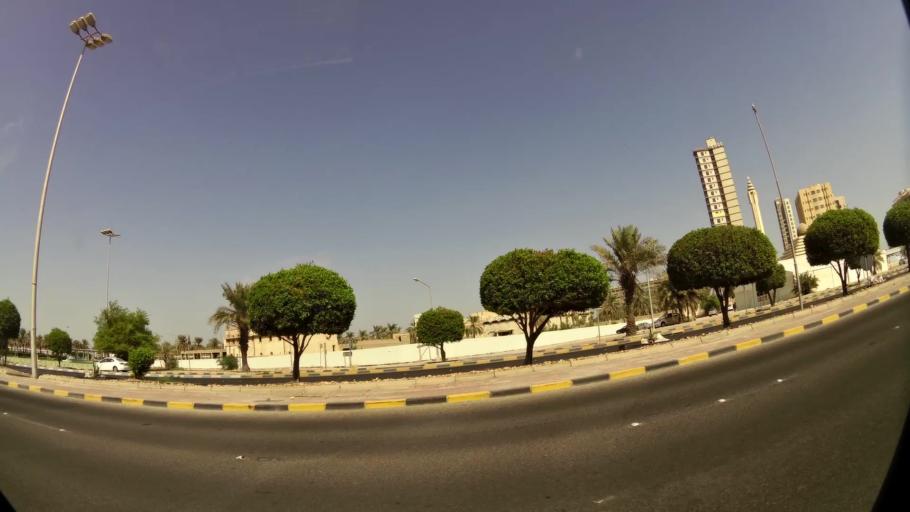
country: KW
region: Muhafazat Hawalli
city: As Salimiyah
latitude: 29.3483
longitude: 48.0922
